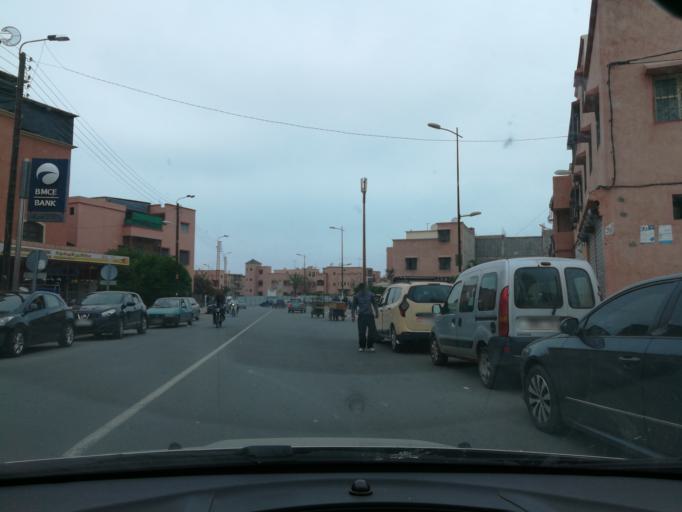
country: MA
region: Marrakech-Tensift-Al Haouz
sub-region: Marrakech
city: Marrakesh
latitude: 31.6593
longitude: -7.9969
